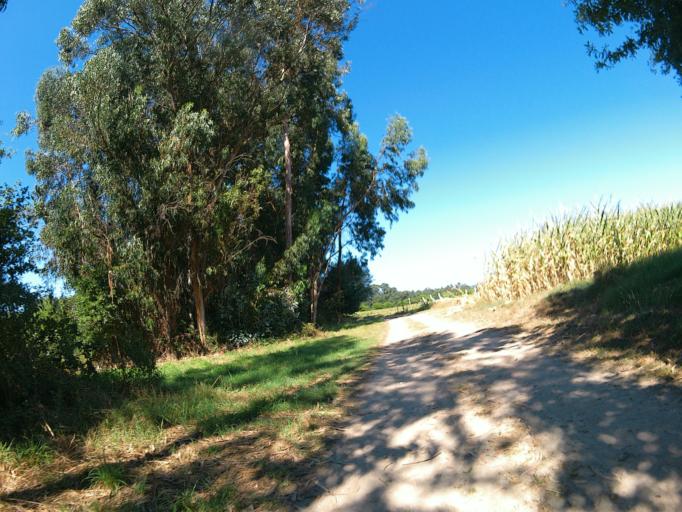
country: PT
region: Viana do Castelo
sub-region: Ponte de Lima
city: Ponte de Lima
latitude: 41.7560
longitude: -8.6236
